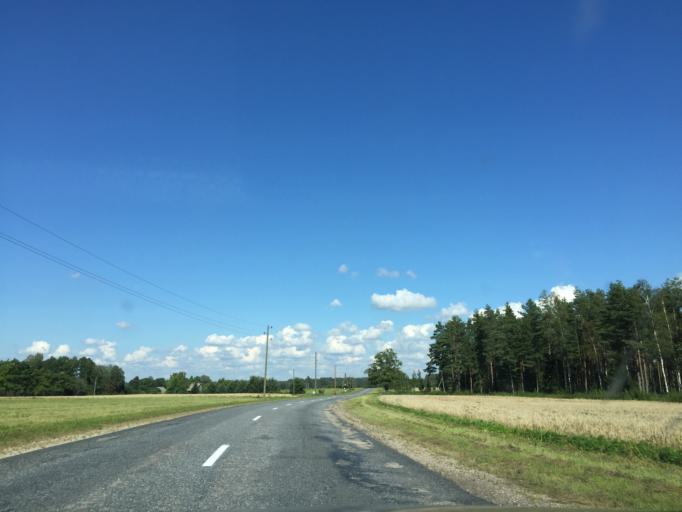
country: LV
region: Limbazu Rajons
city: Limbazi
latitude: 57.4270
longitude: 24.7089
